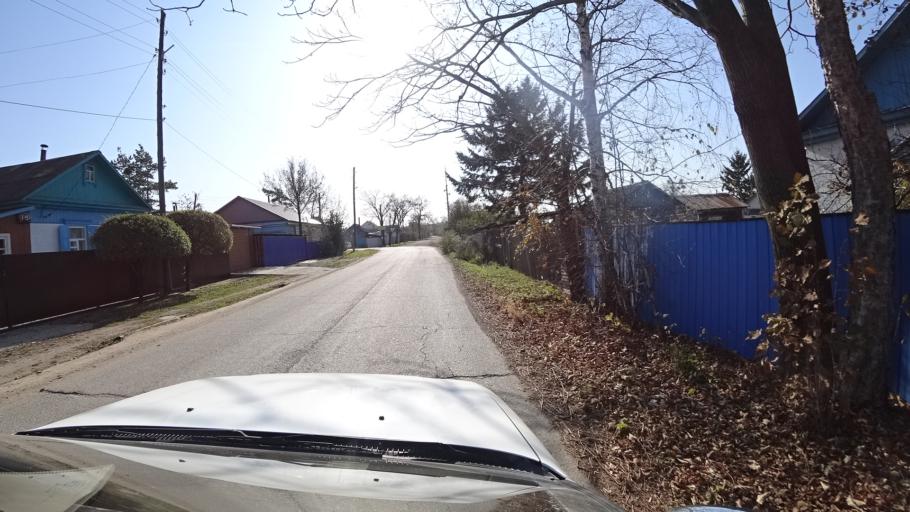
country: RU
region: Primorskiy
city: Dal'nerechensk
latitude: 45.9271
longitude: 133.7212
